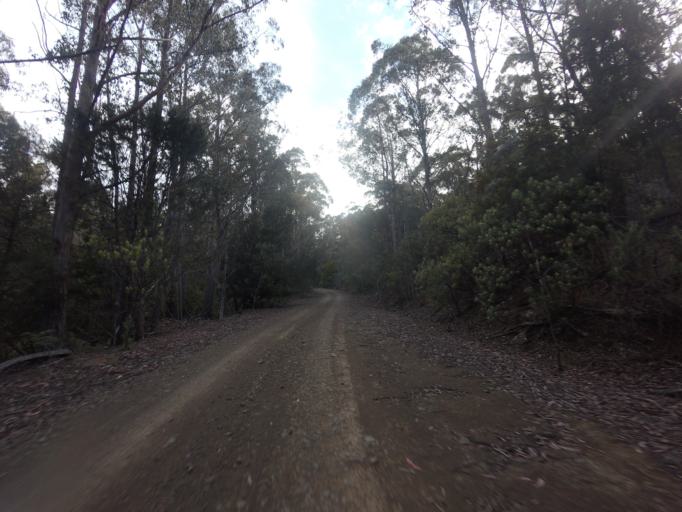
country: AU
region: Tasmania
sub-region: Break O'Day
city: St Helens
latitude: -41.8420
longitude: 148.0624
